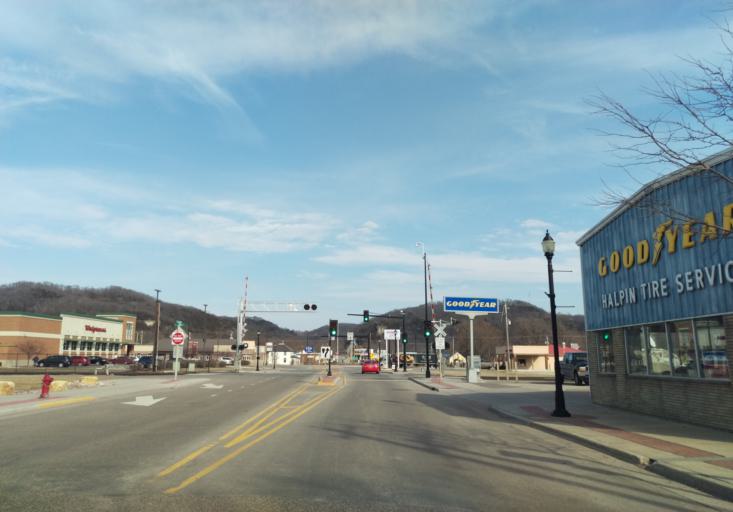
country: US
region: Wisconsin
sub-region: Crawford County
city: Prairie du Chien
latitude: 43.0518
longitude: -91.1431
